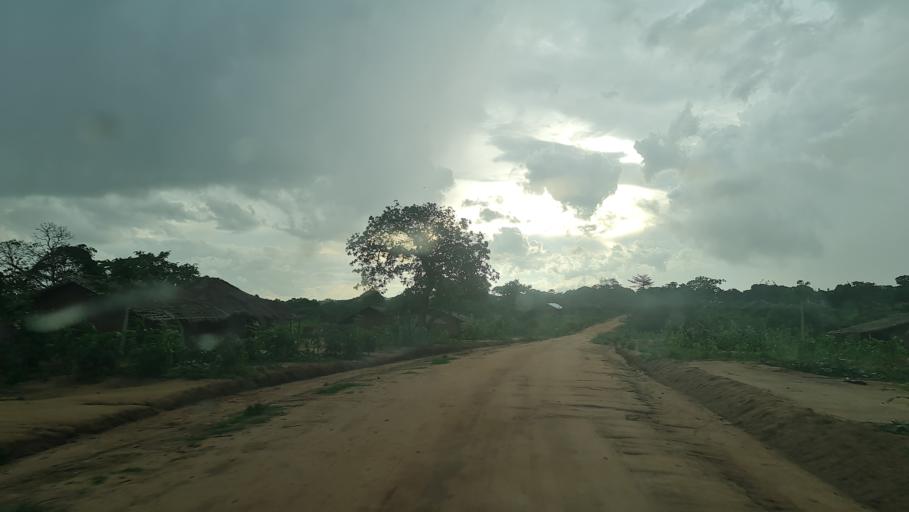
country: MZ
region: Nampula
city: Nacala
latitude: -14.0046
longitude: 40.3556
